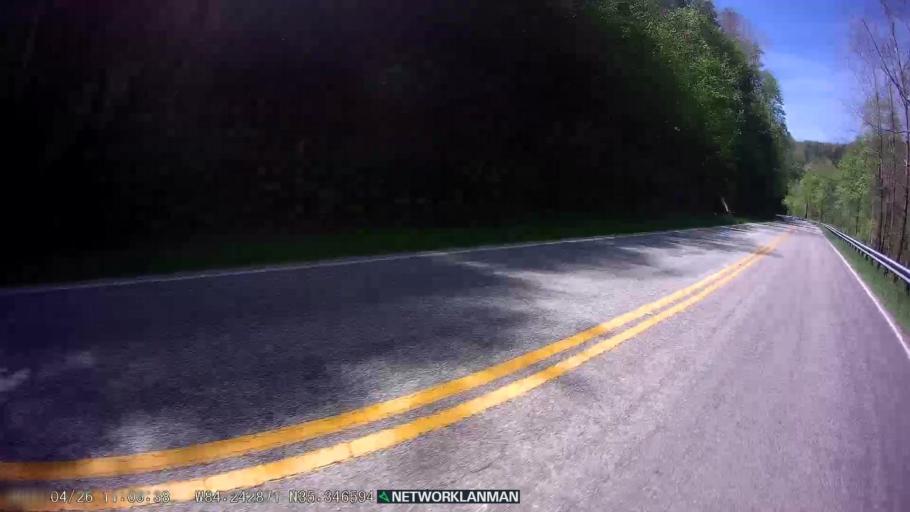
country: US
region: Tennessee
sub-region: Monroe County
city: Madisonville
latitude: 35.3468
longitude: -84.2430
